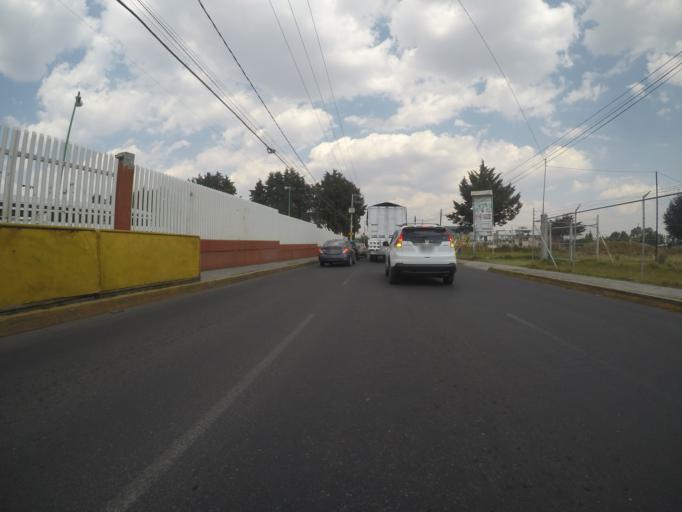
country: MX
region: Mexico
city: San Buenaventura
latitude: 19.2565
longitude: -99.6620
